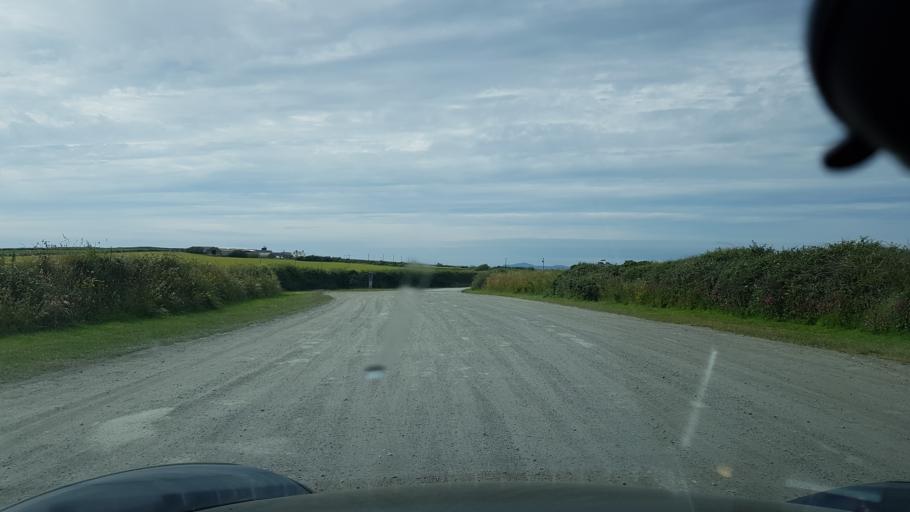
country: GB
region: Wales
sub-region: Pembrokeshire
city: Dale
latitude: 51.7289
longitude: -5.2173
